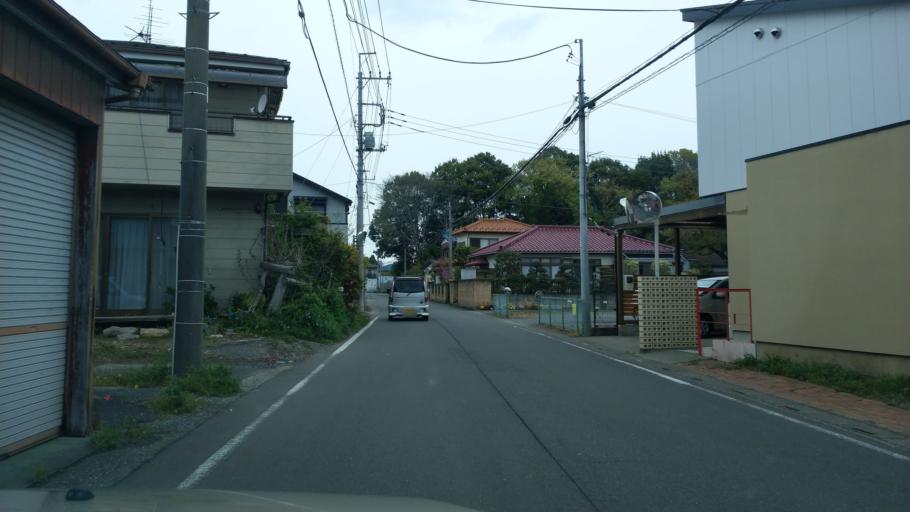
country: JP
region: Saitama
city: Ageoshimo
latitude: 35.9370
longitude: 139.5844
